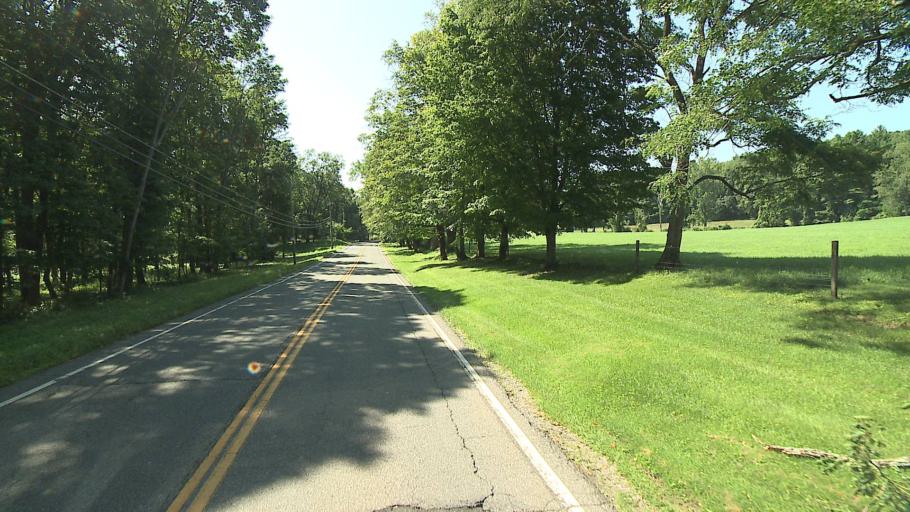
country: US
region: Connecticut
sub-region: Litchfield County
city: Canaan
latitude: 42.0047
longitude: -73.4245
